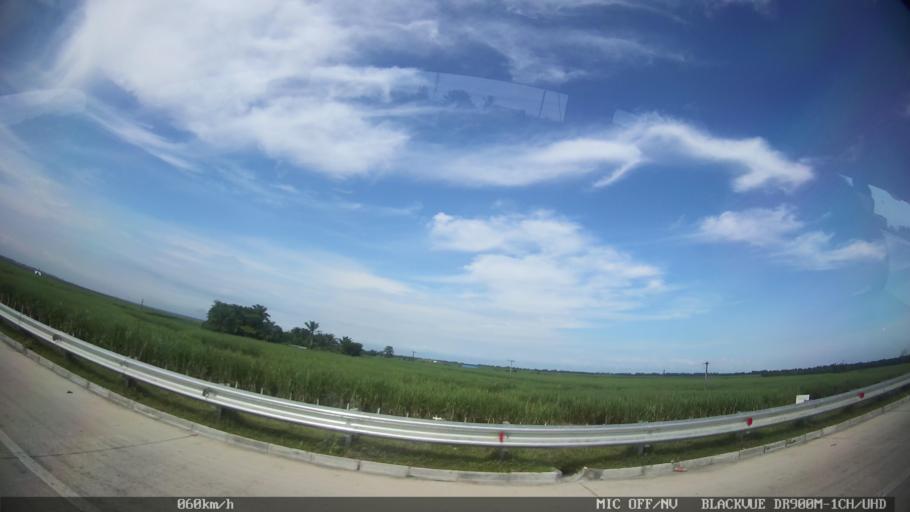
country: ID
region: North Sumatra
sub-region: Kabupaten Langkat
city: Stabat
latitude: 3.7208
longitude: 98.4935
